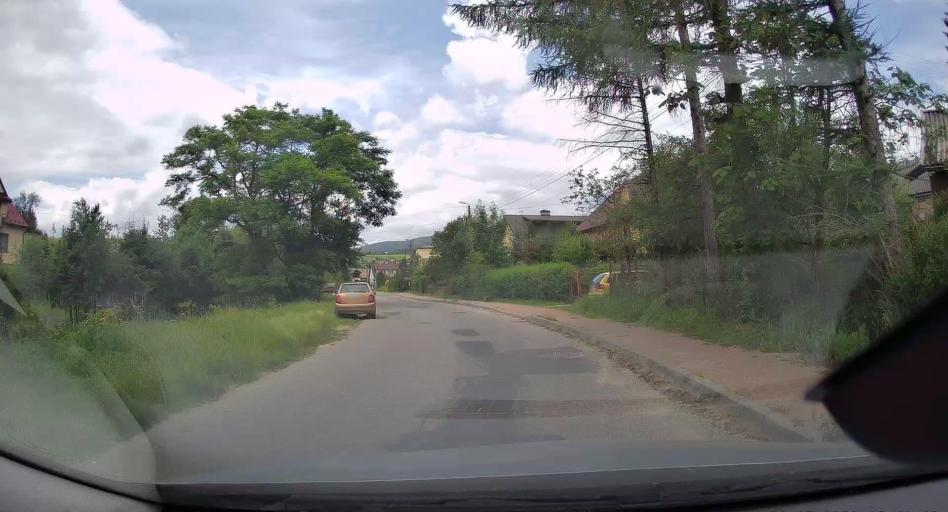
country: PL
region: Lesser Poland Voivodeship
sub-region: Powiat nowosadecki
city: Muszyna
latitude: 49.3666
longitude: 20.8895
